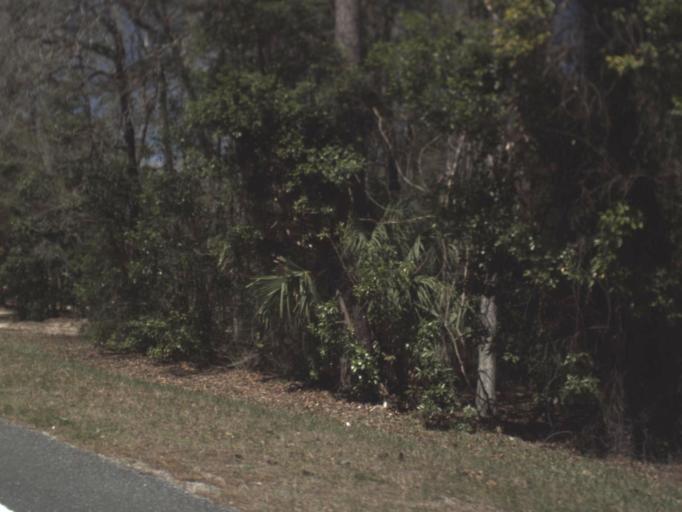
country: US
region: Florida
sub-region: Leon County
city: Woodville
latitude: 30.2426
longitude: -84.2791
